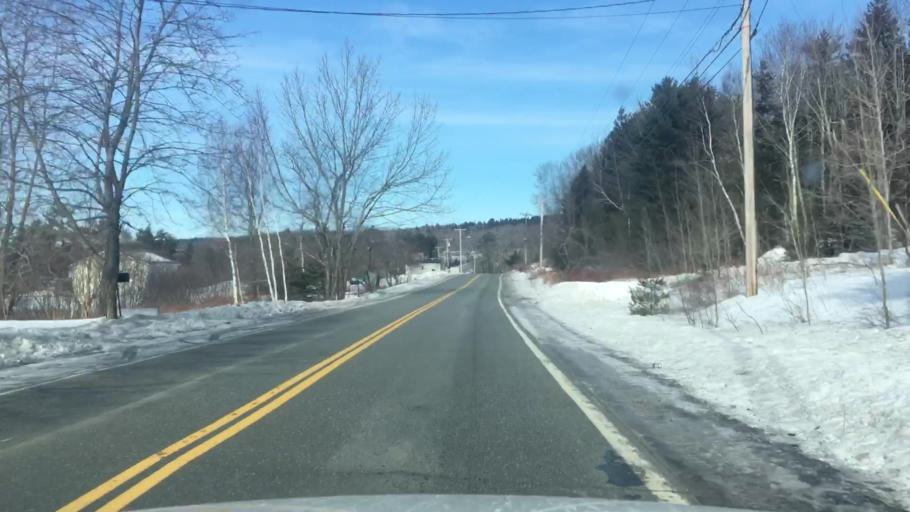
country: US
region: Maine
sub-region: Hancock County
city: Orland
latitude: 44.5480
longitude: -68.7425
